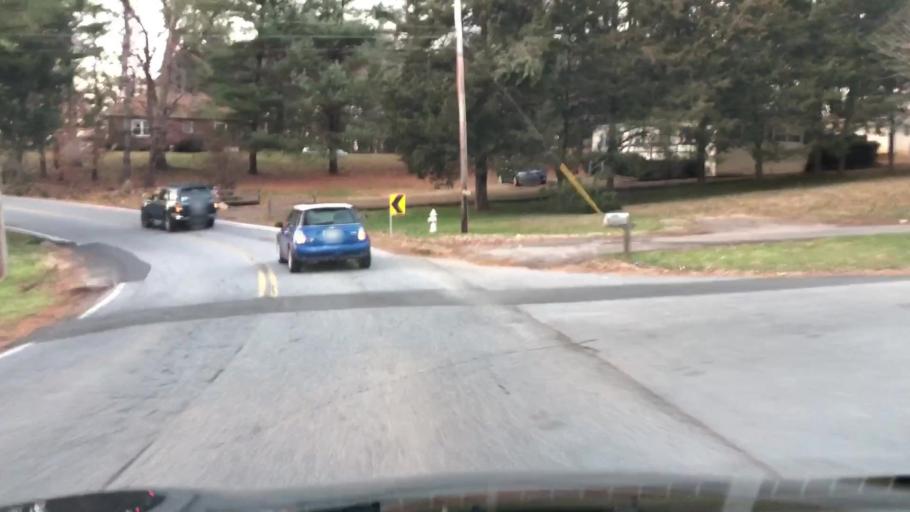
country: US
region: Virginia
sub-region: City of Lynchburg
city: West Lynchburg
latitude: 37.4113
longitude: -79.2248
